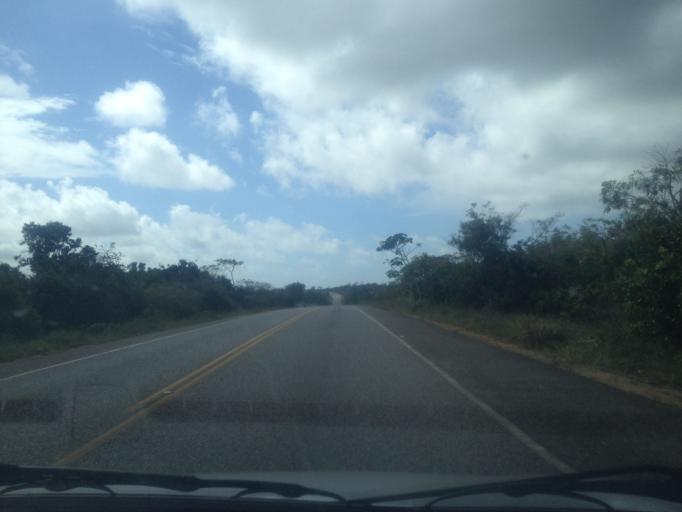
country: BR
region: Bahia
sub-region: Entre Rios
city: Entre Rios
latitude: -12.2436
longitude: -37.8544
